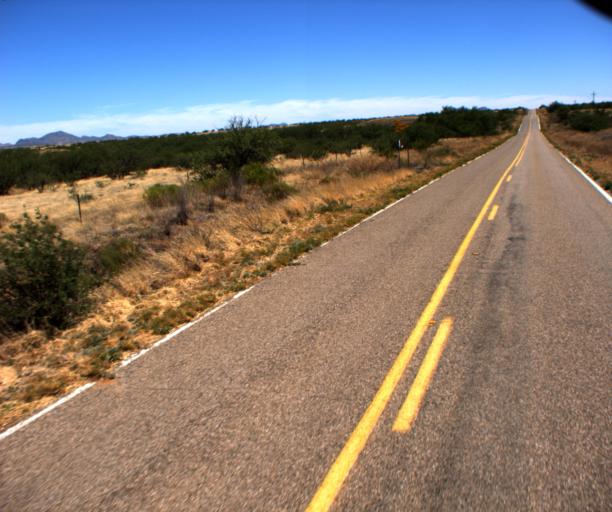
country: US
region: Arizona
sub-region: Pima County
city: Sells
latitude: 31.5617
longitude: -111.5388
